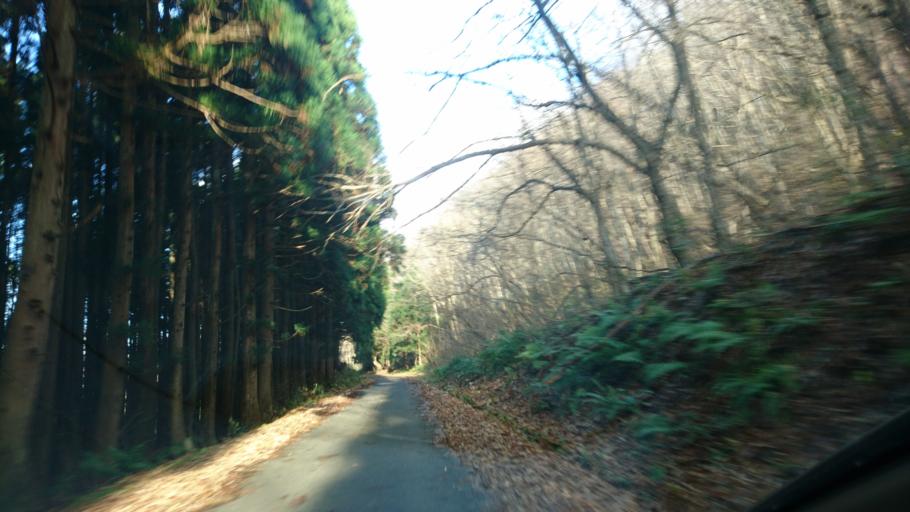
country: JP
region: Akita
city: Kakunodatemachi
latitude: 39.4784
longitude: 140.8045
